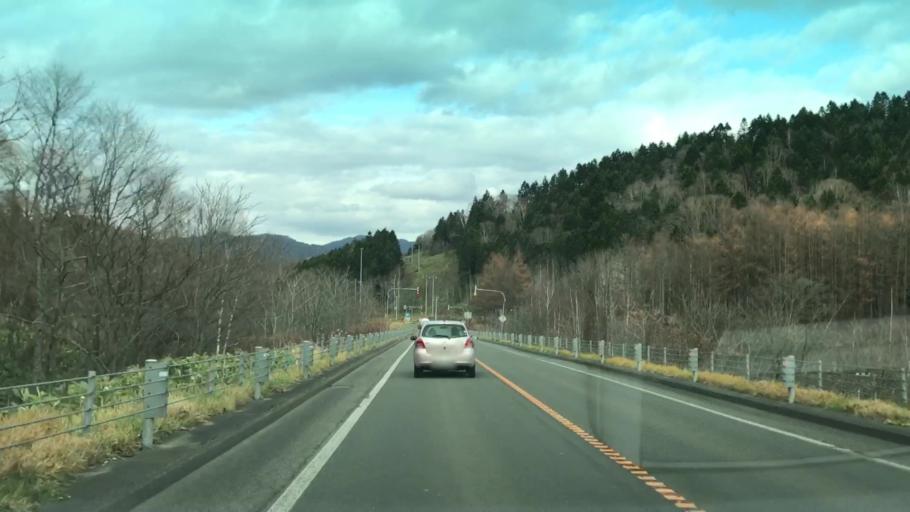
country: JP
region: Hokkaido
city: Shimo-furano
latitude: 42.9235
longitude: 142.4446
